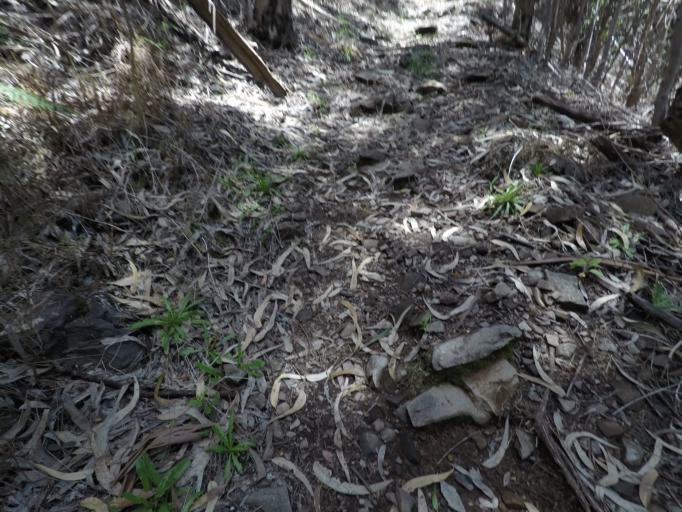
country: PT
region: Madeira
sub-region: Camara de Lobos
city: Curral das Freiras
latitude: 32.7530
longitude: -16.9720
